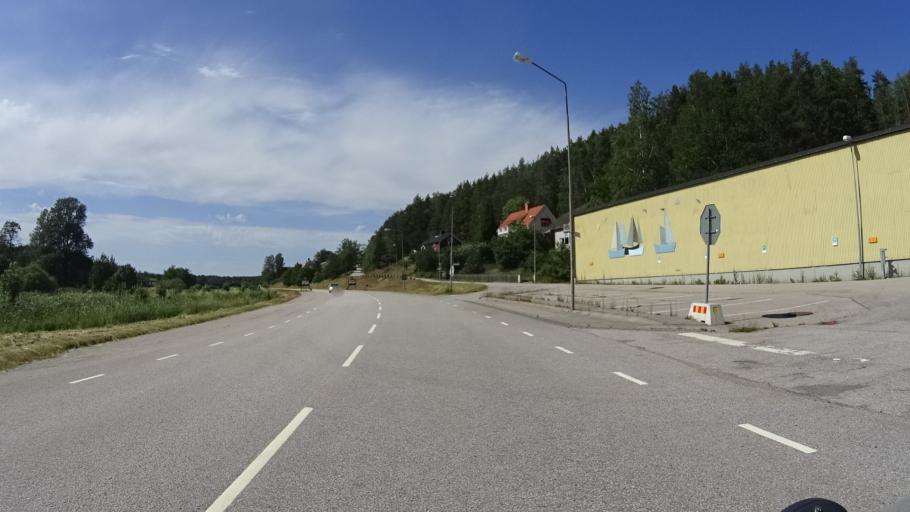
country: SE
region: Kalmar
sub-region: Vasterviks Kommun
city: Gamleby
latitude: 57.9039
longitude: 16.3976
